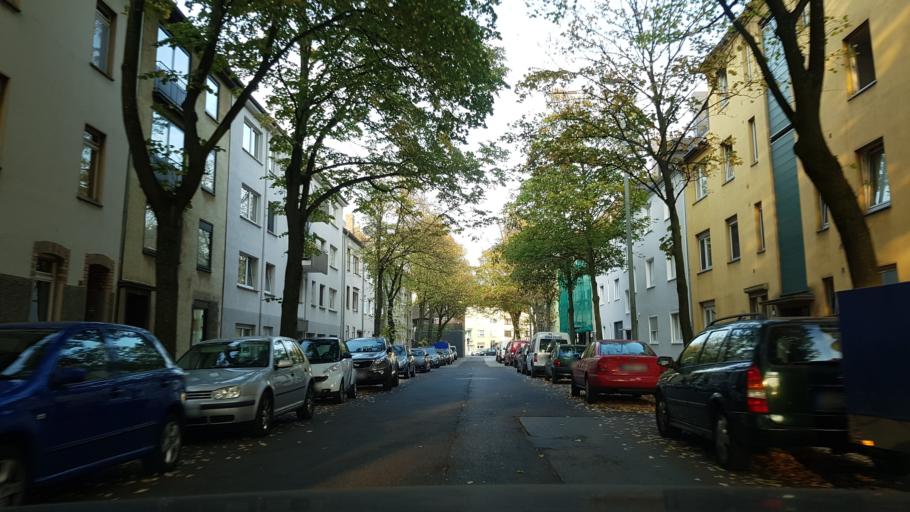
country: DE
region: North Rhine-Westphalia
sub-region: Regierungsbezirk Dusseldorf
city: Hochfeld
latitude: 51.4144
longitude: 6.7602
